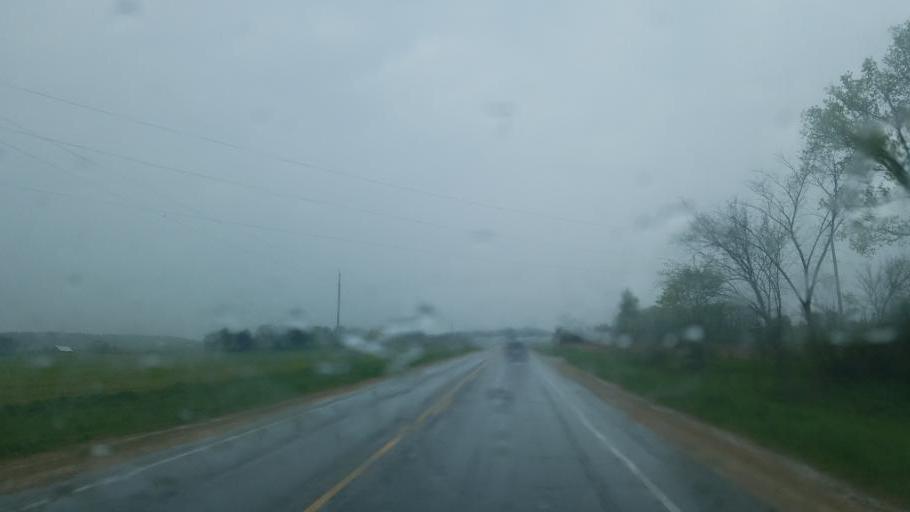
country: US
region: Wisconsin
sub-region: Sauk County
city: Reedsburg
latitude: 43.5621
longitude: -90.0749
